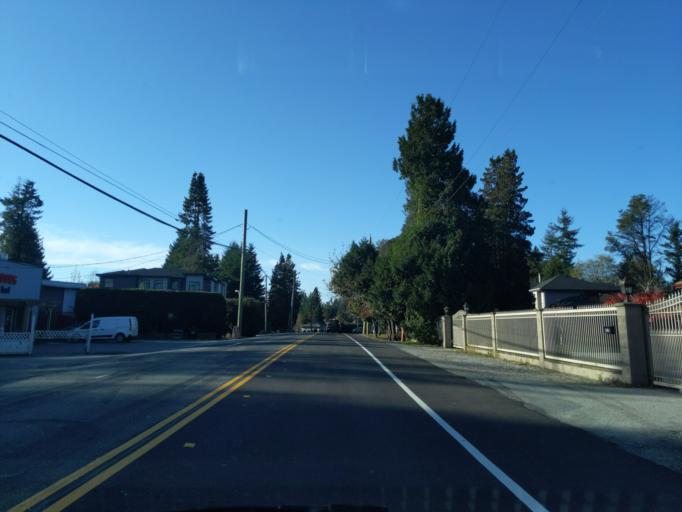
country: CA
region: British Columbia
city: New Westminster
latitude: 49.1886
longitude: -122.8595
